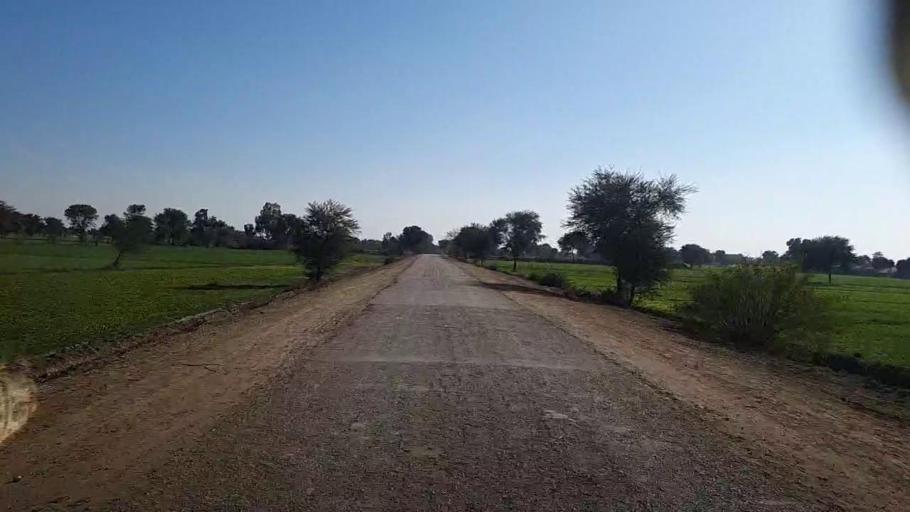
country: PK
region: Sindh
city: Khairpur
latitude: 27.9161
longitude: 69.7517
